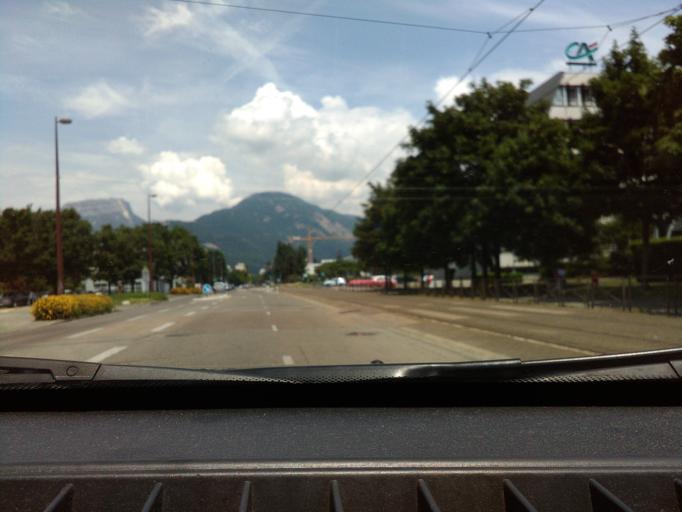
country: FR
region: Rhone-Alpes
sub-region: Departement de l'Isere
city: Grenoble
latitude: 45.1706
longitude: 5.7321
